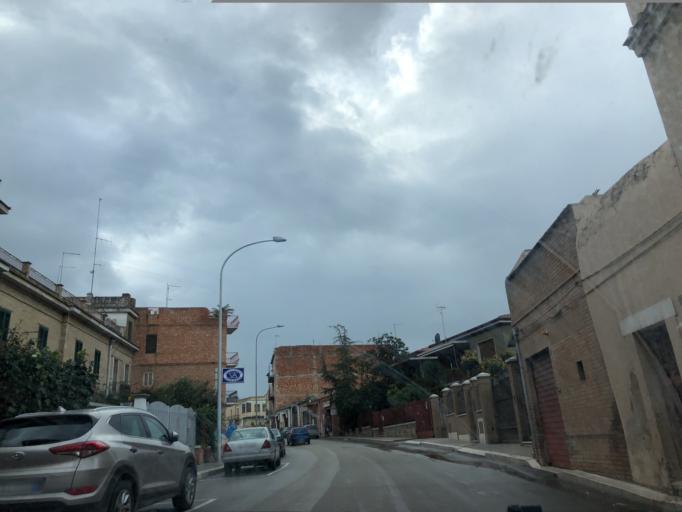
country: IT
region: Apulia
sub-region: Provincia di Foggia
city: Lucera
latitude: 41.5067
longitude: 15.3395
